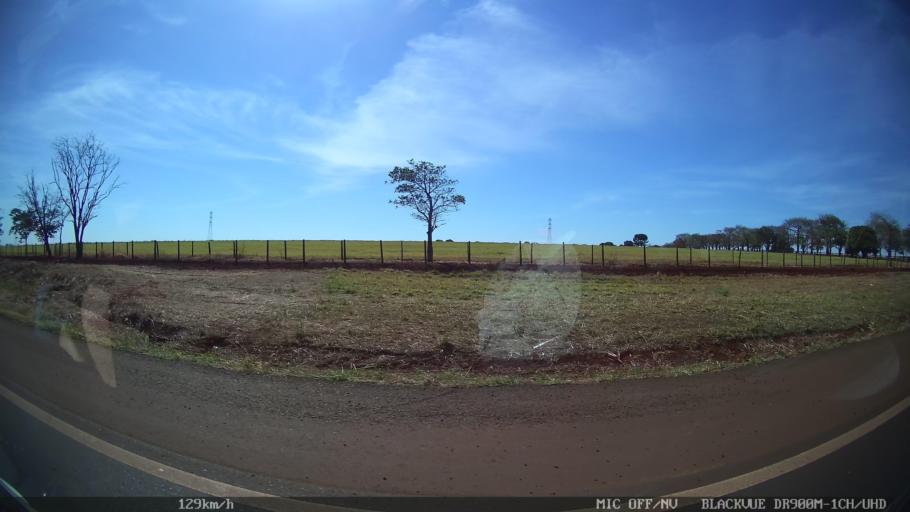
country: BR
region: Sao Paulo
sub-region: Ipua
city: Ipua
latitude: -20.4738
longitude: -48.0997
